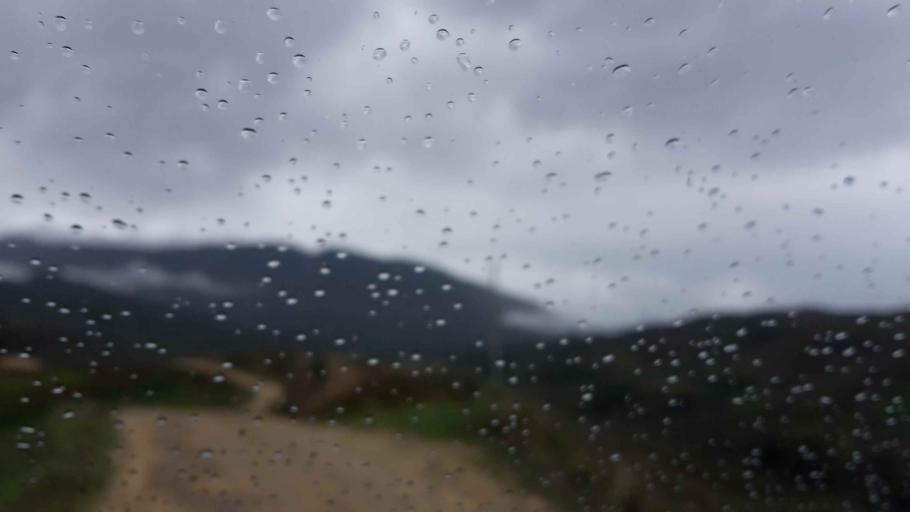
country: BO
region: Cochabamba
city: Cochabamba
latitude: -17.1412
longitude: -66.1033
